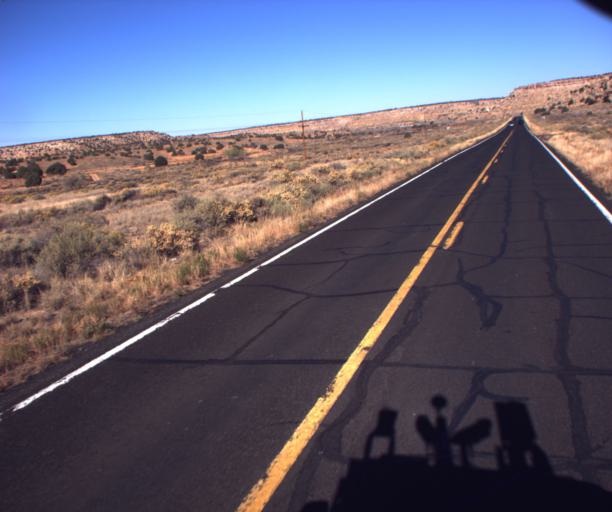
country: US
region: Arizona
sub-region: Navajo County
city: First Mesa
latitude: 35.8287
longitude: -110.2231
